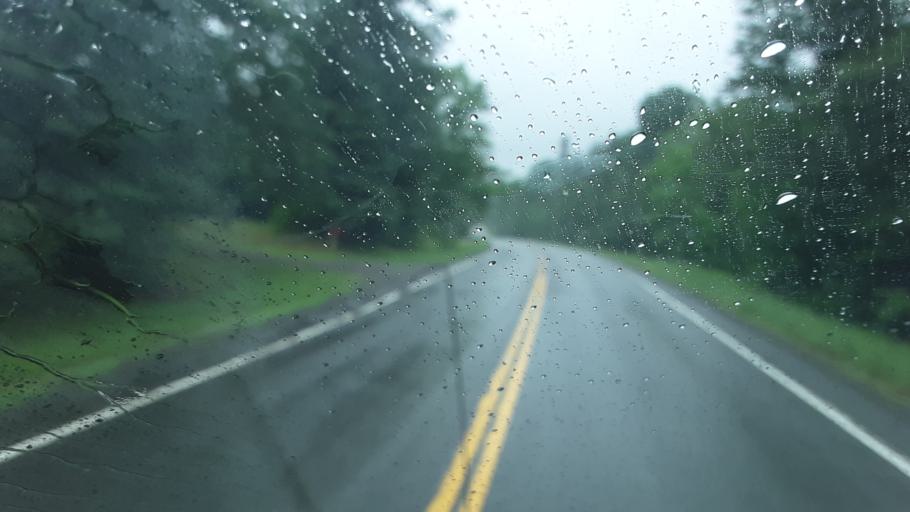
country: US
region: Maine
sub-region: Penobscot County
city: Patten
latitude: 46.1849
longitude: -68.3342
